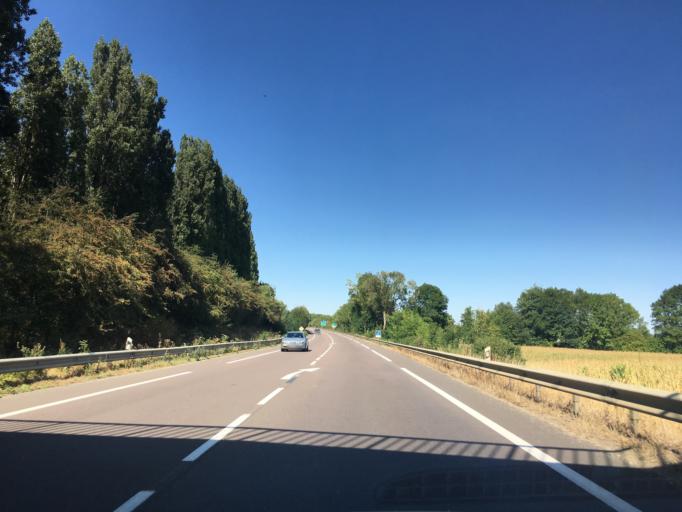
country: FR
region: Bourgogne
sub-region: Departement de l'Yonne
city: Maillot
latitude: 48.1855
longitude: 3.3072
